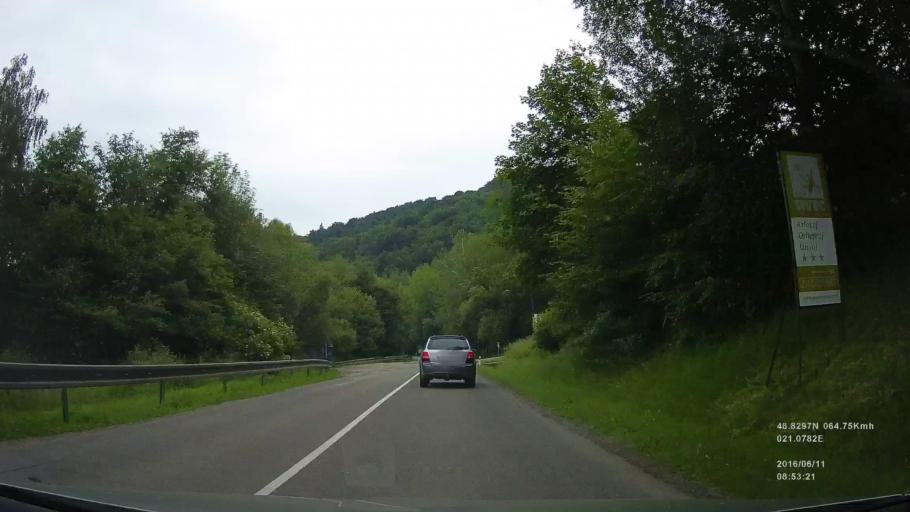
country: SK
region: Kosicky
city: Gelnica
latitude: 48.8249
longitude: 21.0813
